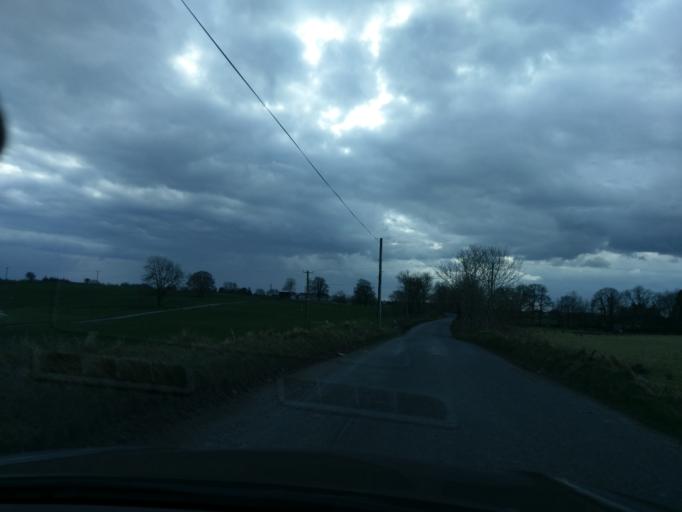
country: IE
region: Connaught
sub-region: County Galway
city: Athenry
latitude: 53.4923
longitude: -8.6094
